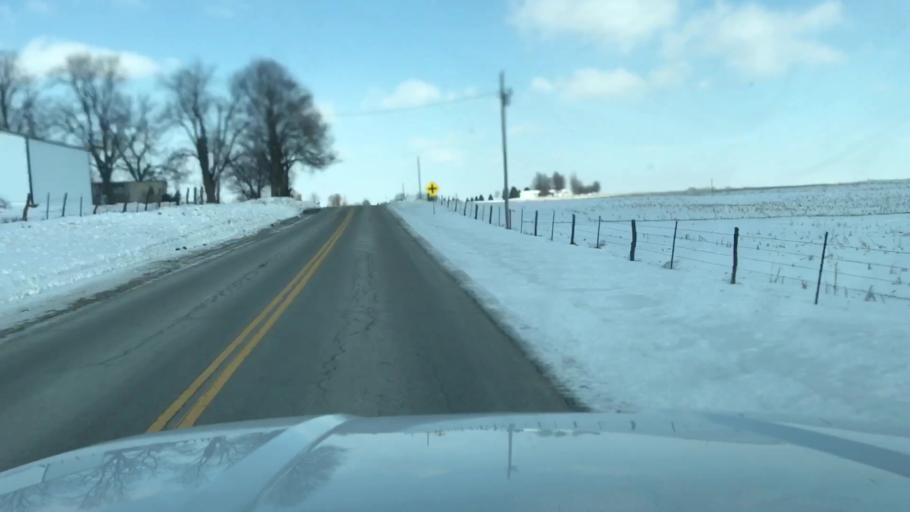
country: US
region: Missouri
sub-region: Nodaway County
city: Maryville
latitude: 40.3563
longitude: -94.7221
